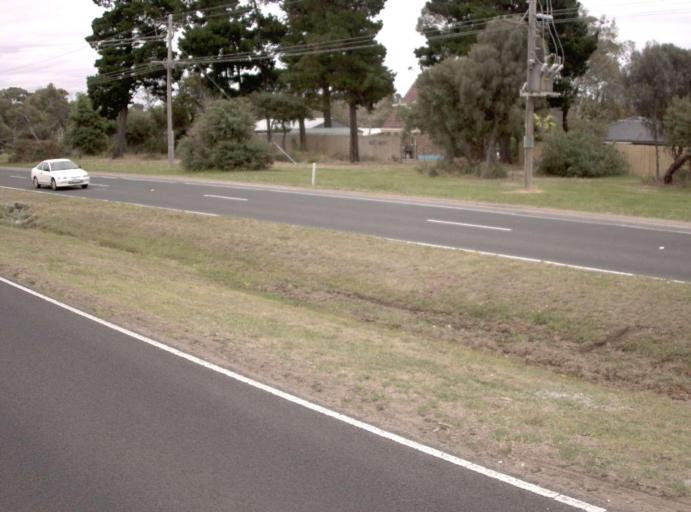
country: AU
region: Victoria
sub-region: Mornington Peninsula
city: Mount Martha
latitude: -38.2472
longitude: 145.0373
